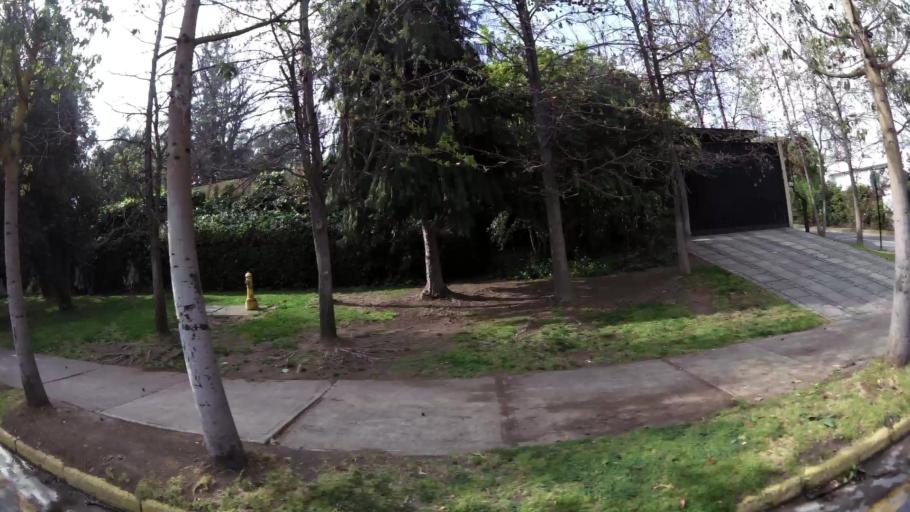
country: CL
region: Santiago Metropolitan
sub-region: Provincia de Santiago
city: Villa Presidente Frei, Nunoa, Santiago, Chile
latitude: -33.3756
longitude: -70.5285
